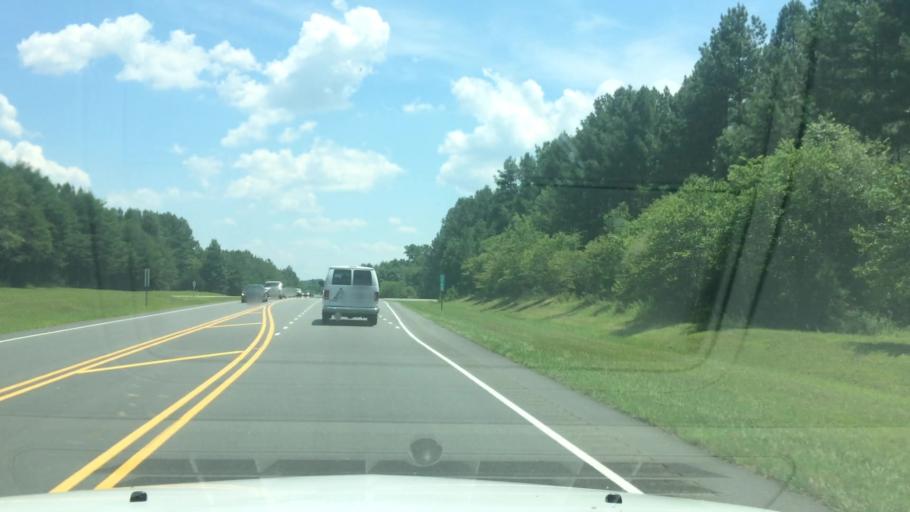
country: US
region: North Carolina
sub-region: Iredell County
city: Statesville
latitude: 35.8099
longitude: -80.9728
